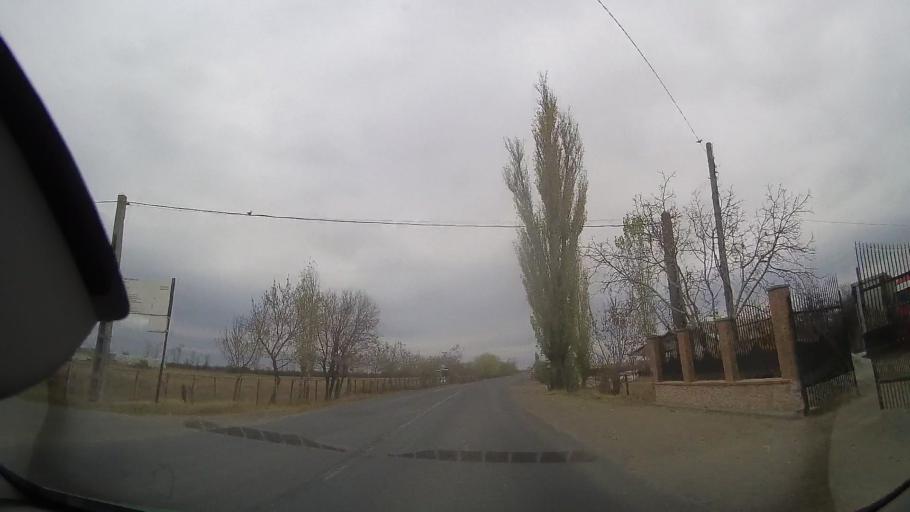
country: RO
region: Buzau
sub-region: Comuna Padina
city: Padina
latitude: 44.8206
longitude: 27.1185
